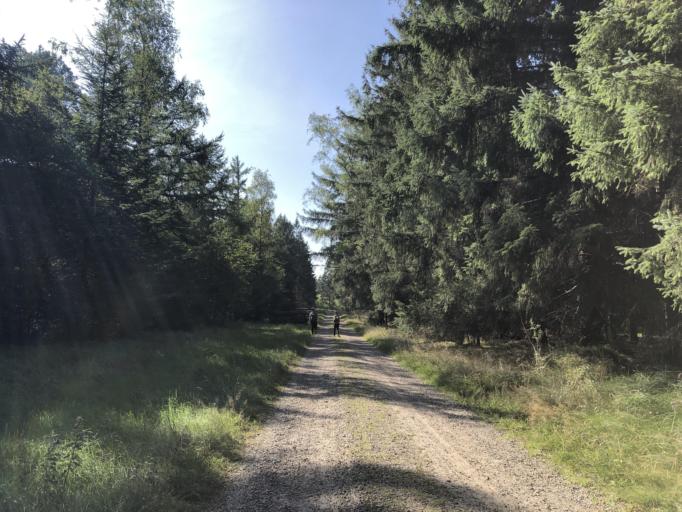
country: DK
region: Central Jutland
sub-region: Lemvig Kommune
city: Lemvig
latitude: 56.4717
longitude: 8.3181
